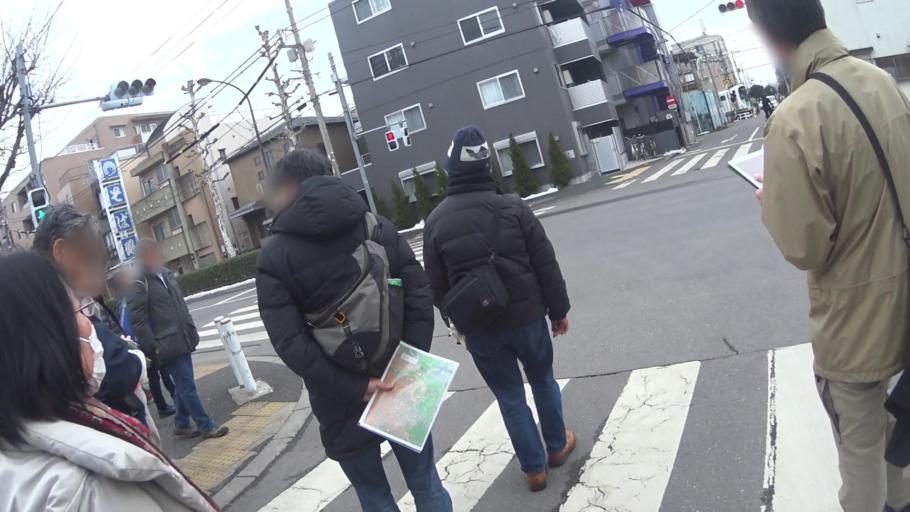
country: JP
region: Tokyo
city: Musashino
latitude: 35.7258
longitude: 139.6017
